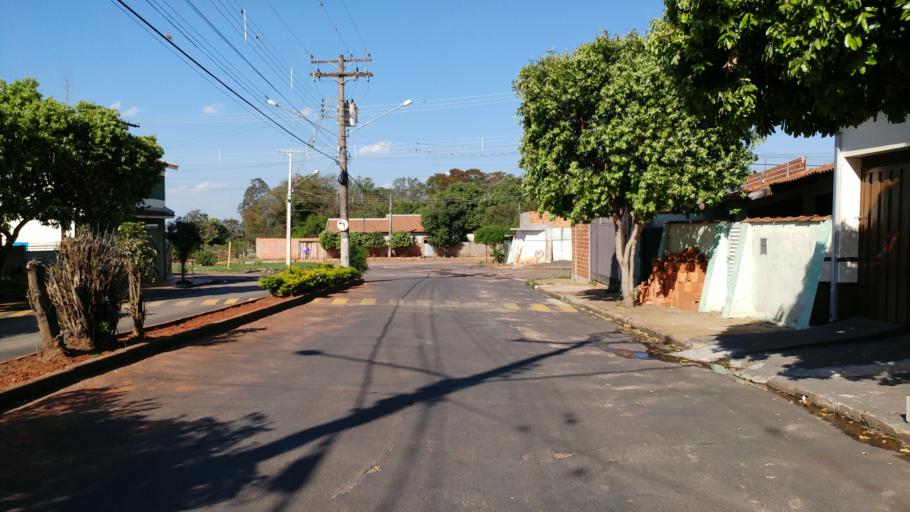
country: BR
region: Sao Paulo
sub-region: Paraguacu Paulista
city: Paraguacu Paulista
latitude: -22.4272
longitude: -50.5721
